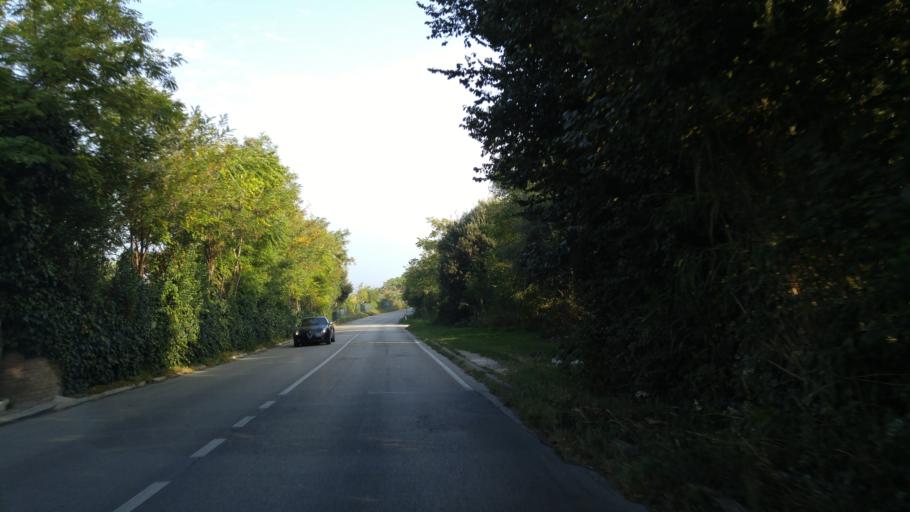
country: IT
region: The Marches
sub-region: Provincia di Pesaro e Urbino
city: Fenile
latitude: 43.8849
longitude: 12.9550
